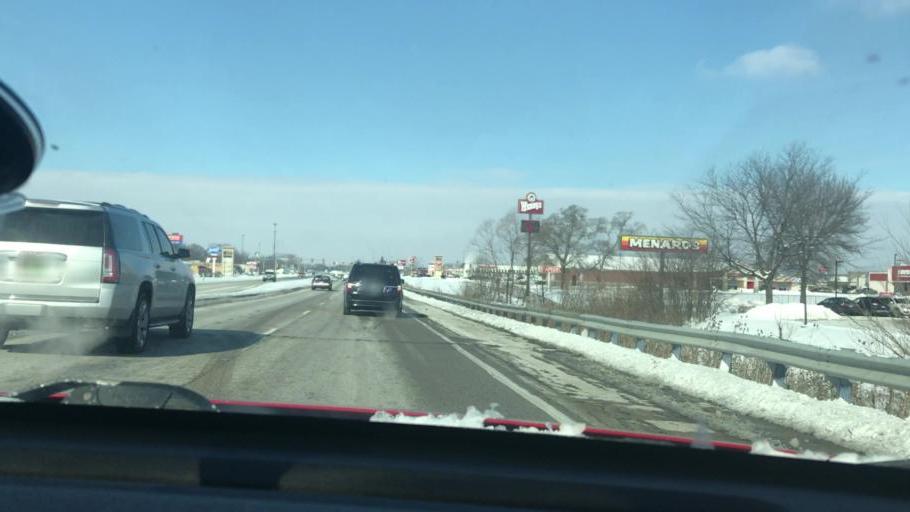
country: US
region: Illinois
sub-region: Tazewell County
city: Pekin
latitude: 40.5418
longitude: -89.5957
